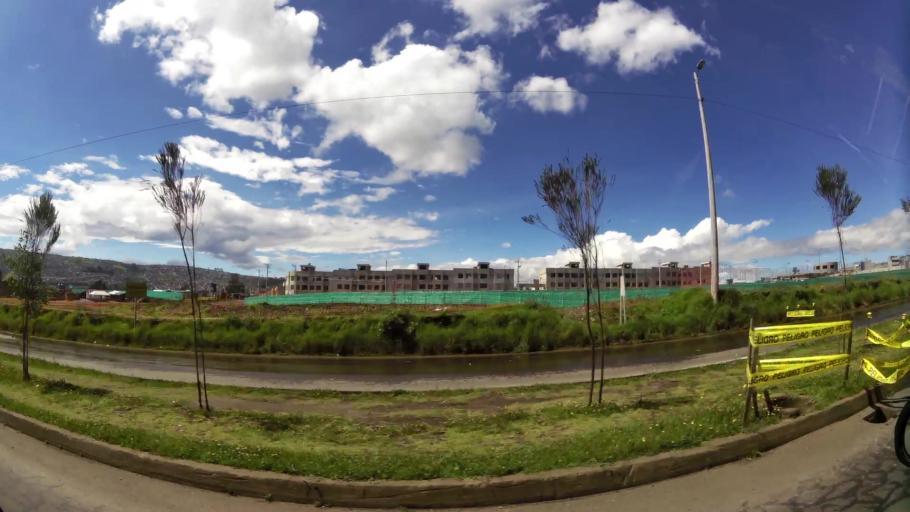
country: EC
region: Pichincha
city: Quito
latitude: -0.2991
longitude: -78.5552
